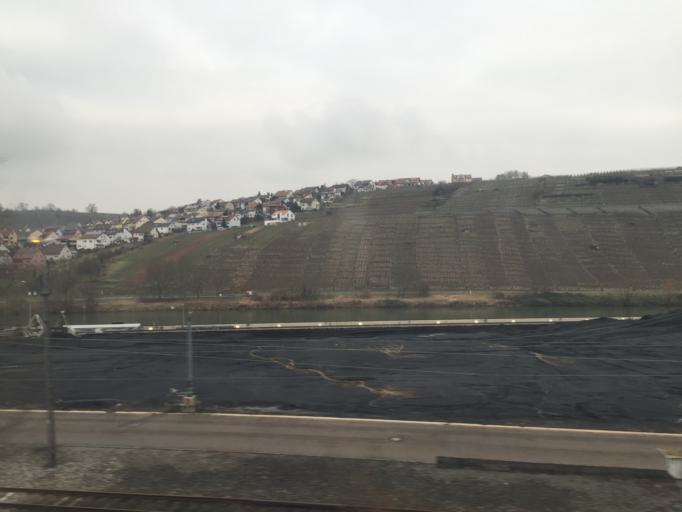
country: DE
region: Baden-Wuerttemberg
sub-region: Regierungsbezirk Stuttgart
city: Walheim
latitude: 49.0195
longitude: 9.1556
